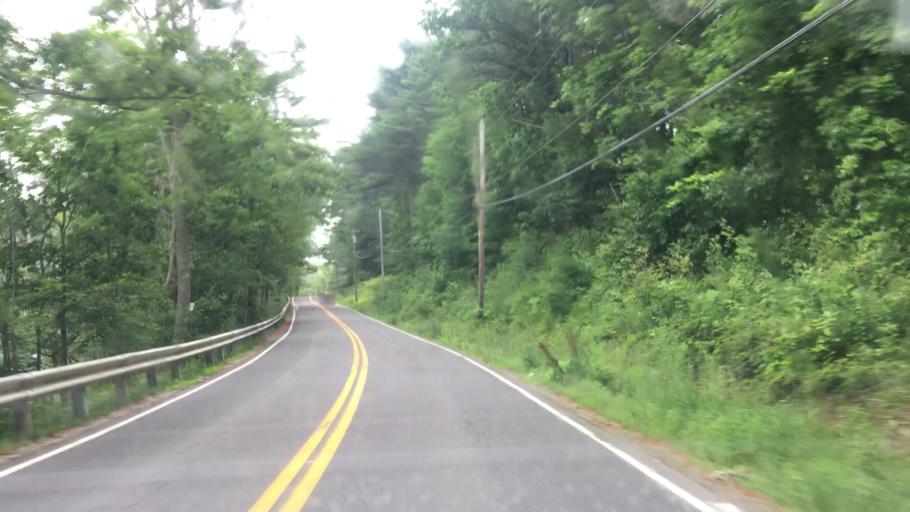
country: US
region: Maine
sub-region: Lincoln County
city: Wiscasset
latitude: 43.9921
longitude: -69.6484
